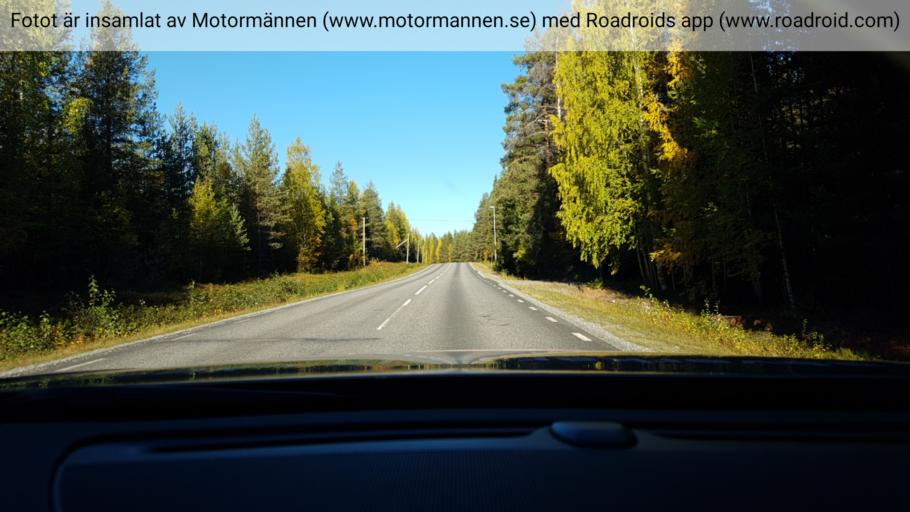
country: SE
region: Norrbotten
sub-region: Pitea Kommun
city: Roknas
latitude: 65.3548
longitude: 21.0850
